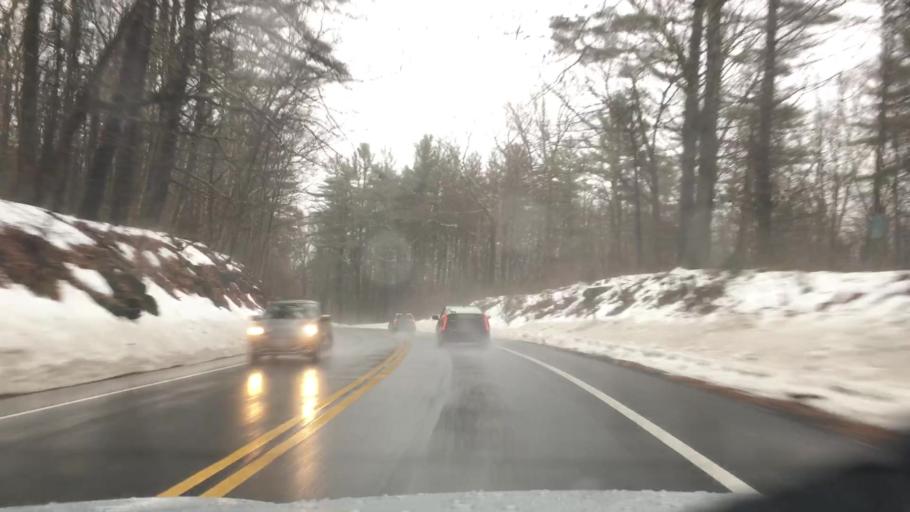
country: US
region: Massachusetts
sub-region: Franklin County
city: Shutesbury
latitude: 42.4350
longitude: -72.3912
